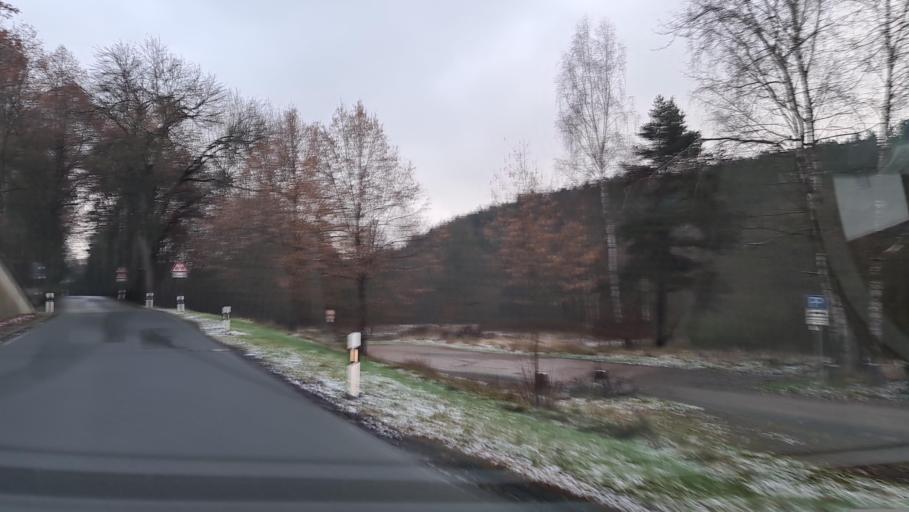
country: DE
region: Saxony
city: Mylau
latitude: 50.5988
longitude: 12.2860
